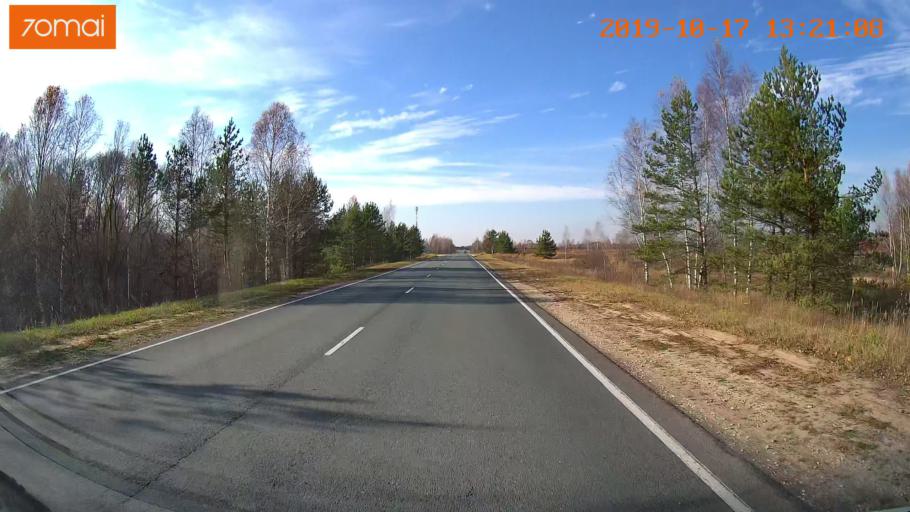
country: RU
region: Rjazan
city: Gus'-Zheleznyy
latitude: 55.0798
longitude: 41.0345
